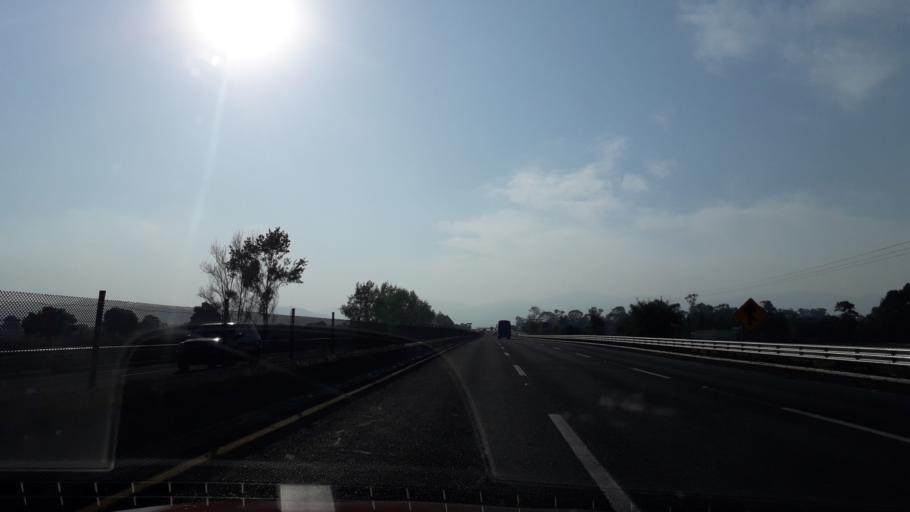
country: MX
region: Puebla
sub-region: Tlahuapan
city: Guadalupe Zaragoza
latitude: 19.3329
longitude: -98.5486
